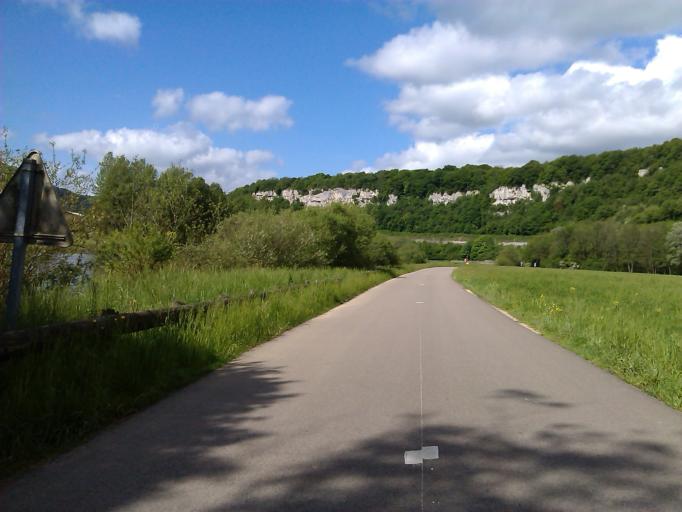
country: FR
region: Franche-Comte
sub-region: Departement du Doubs
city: Roulans
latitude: 47.3211
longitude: 6.2735
